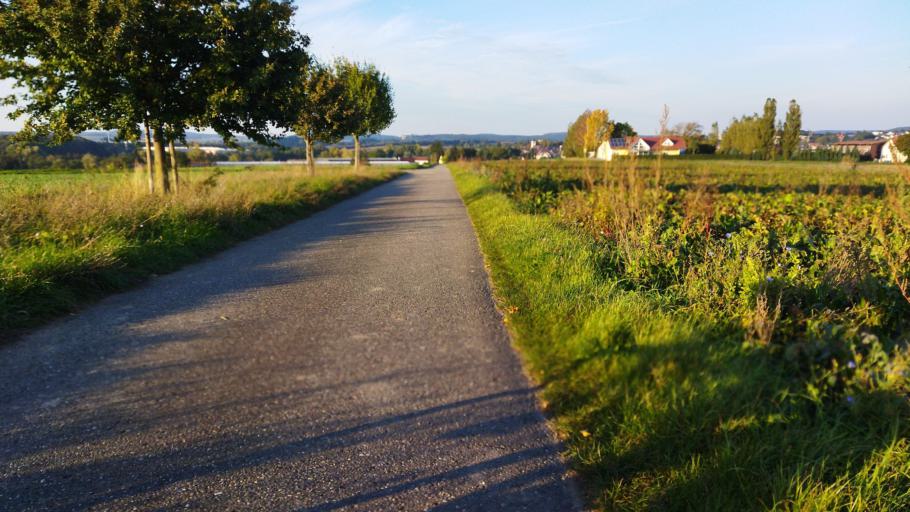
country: DE
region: Baden-Wuerttemberg
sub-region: Regierungsbezirk Stuttgart
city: Abstatt
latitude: 49.0492
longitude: 9.2750
